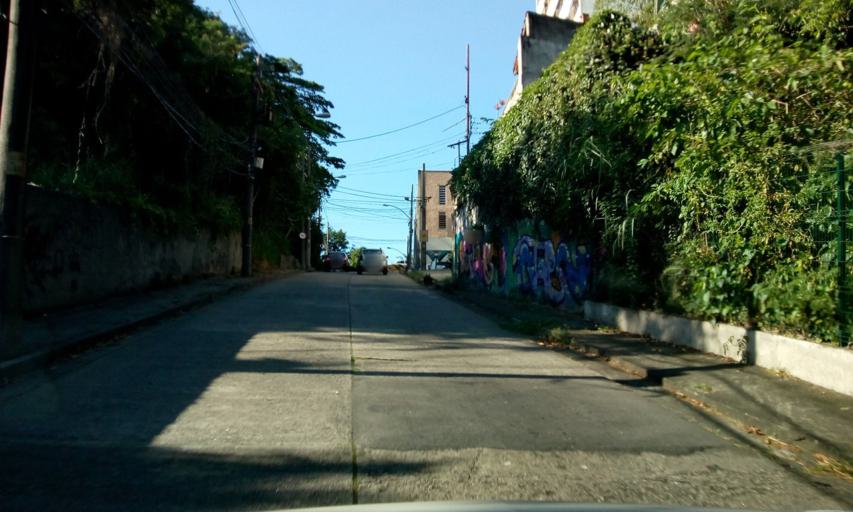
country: BR
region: Rio de Janeiro
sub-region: Rio De Janeiro
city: Rio de Janeiro
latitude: -22.9599
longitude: -43.1786
